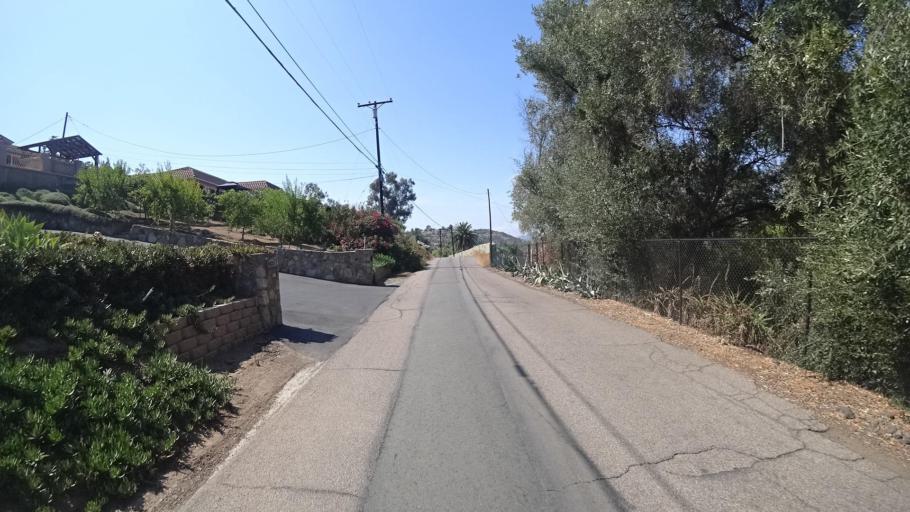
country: US
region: California
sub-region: San Diego County
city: Granite Hills
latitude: 32.7788
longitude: -116.9215
